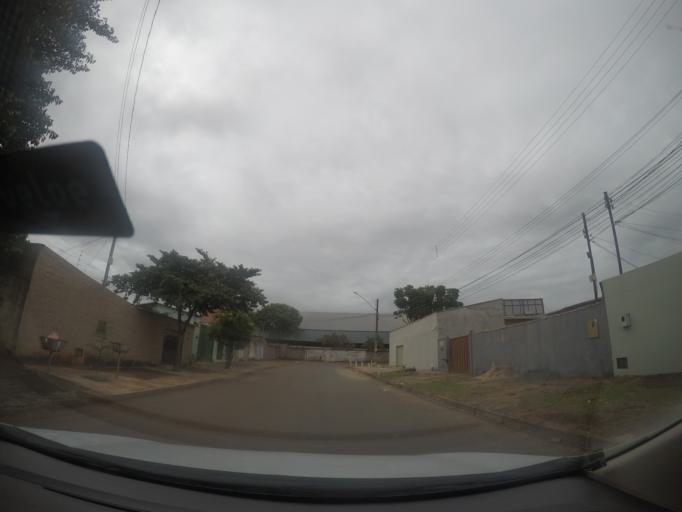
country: BR
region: Goias
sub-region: Goiania
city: Goiania
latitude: -16.7044
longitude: -49.3232
